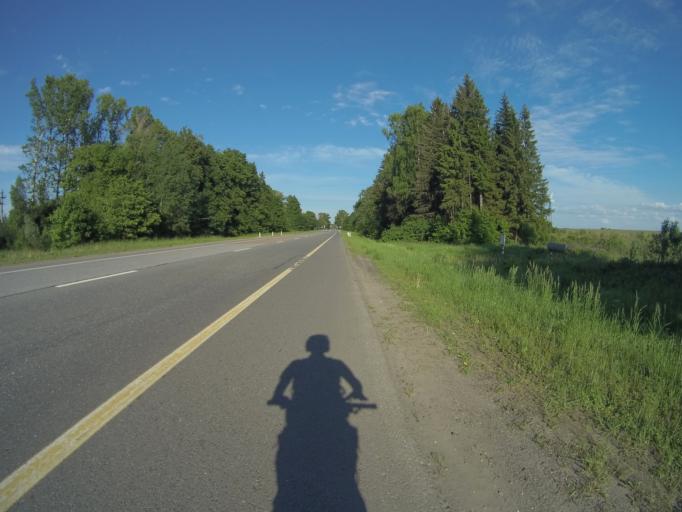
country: RU
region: Vladimir
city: Orgtrud
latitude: 56.1991
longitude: 40.8297
